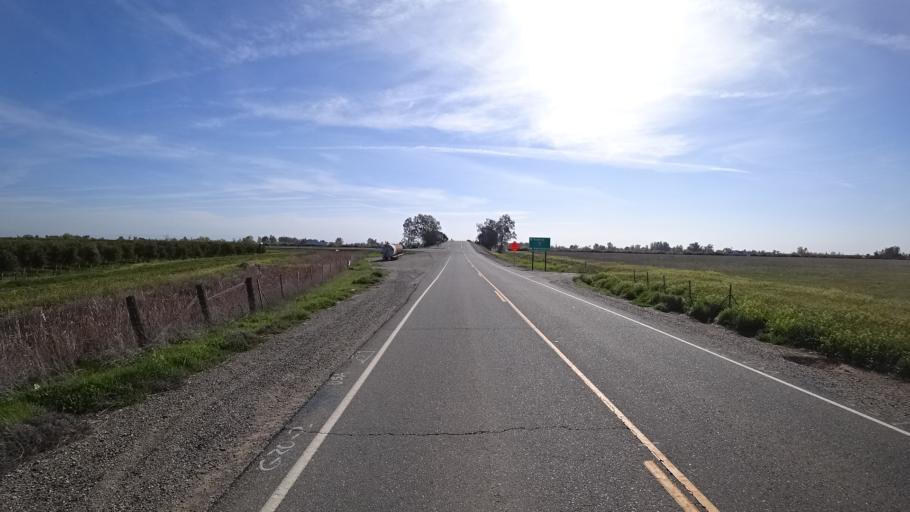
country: US
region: California
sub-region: Glenn County
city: Willows
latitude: 39.6243
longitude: -122.2083
